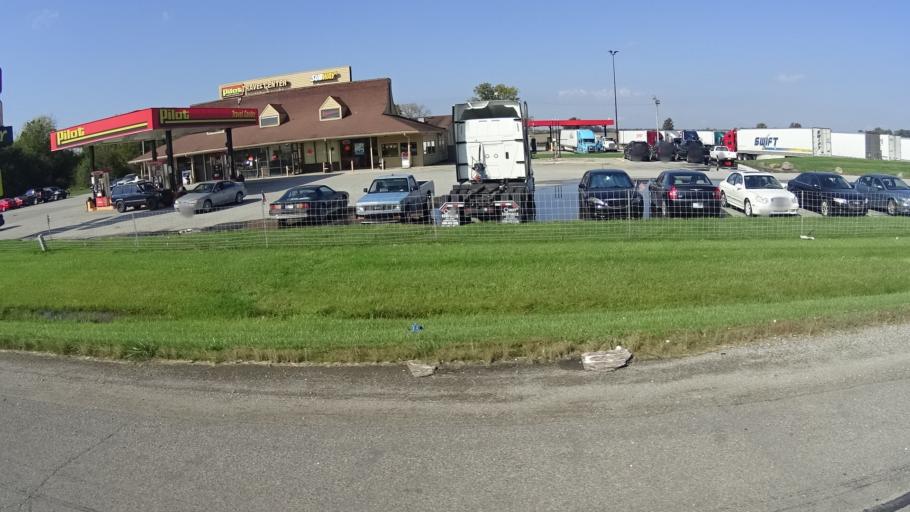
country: US
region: Indiana
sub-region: Madison County
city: Ingalls
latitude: 39.9959
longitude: -85.8432
